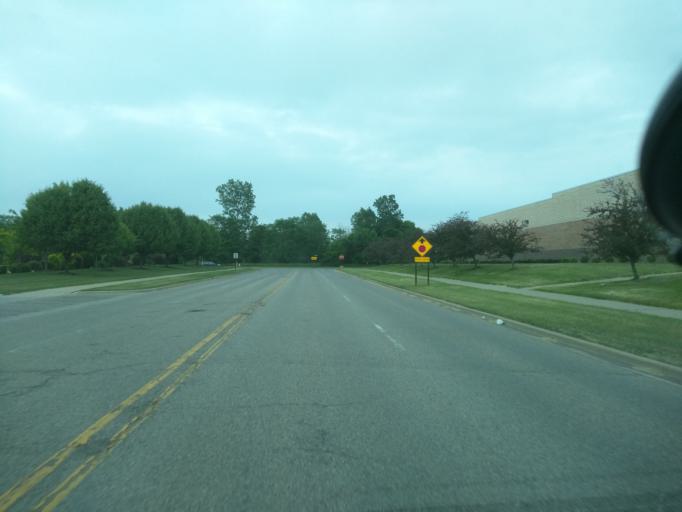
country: US
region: Michigan
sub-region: Ingham County
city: Okemos
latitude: 42.7228
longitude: -84.4118
